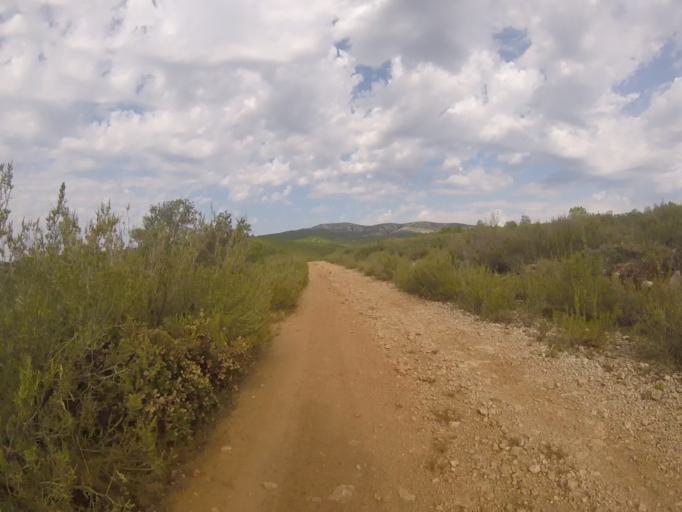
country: ES
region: Valencia
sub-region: Provincia de Castello
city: Alcala de Xivert
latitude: 40.3846
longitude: 0.2105
